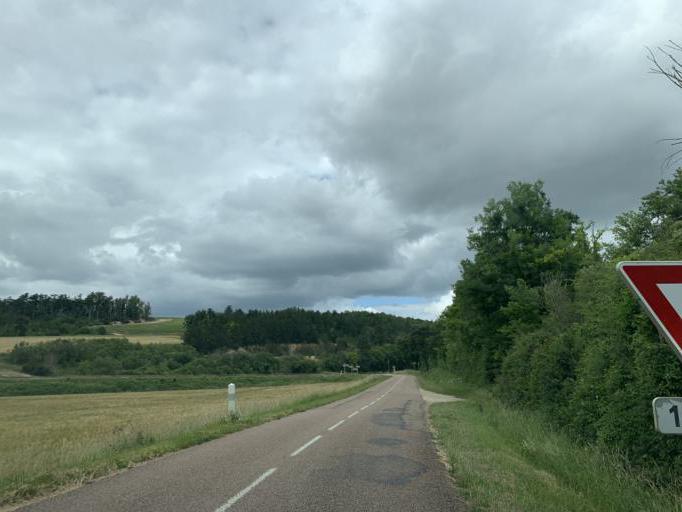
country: FR
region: Bourgogne
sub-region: Departement de l'Yonne
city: Saint-Bris-le-Vineux
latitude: 47.7259
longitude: 3.6938
